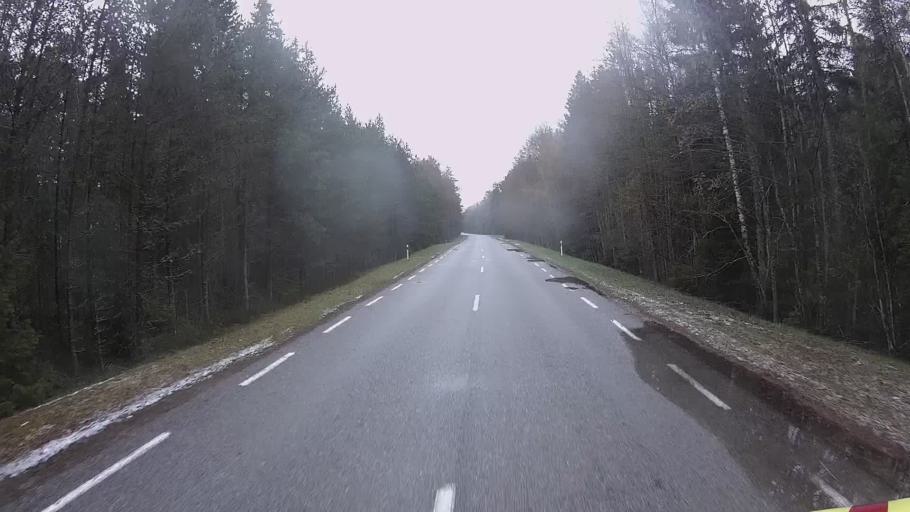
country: EE
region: Hiiumaa
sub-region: Kaerdla linn
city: Kardla
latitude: 59.0607
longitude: 22.6846
